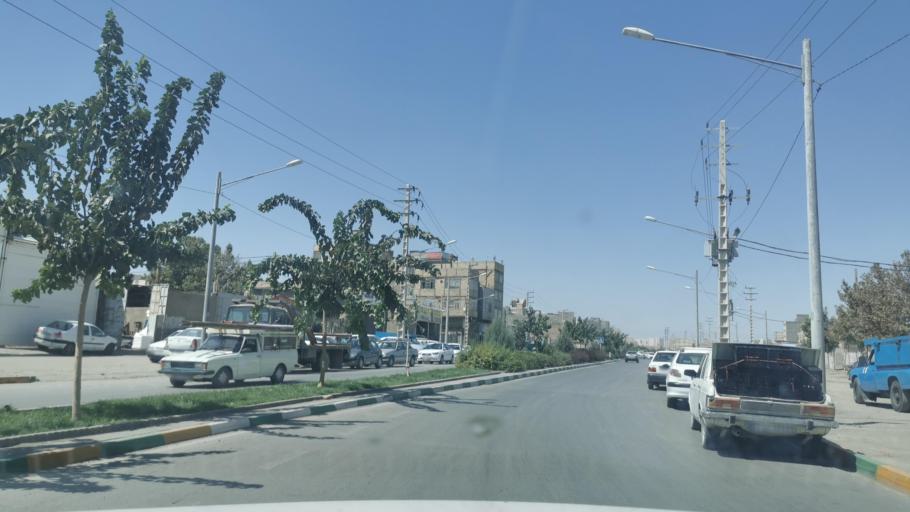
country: IR
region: Razavi Khorasan
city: Mashhad
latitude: 36.3541
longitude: 59.5698
